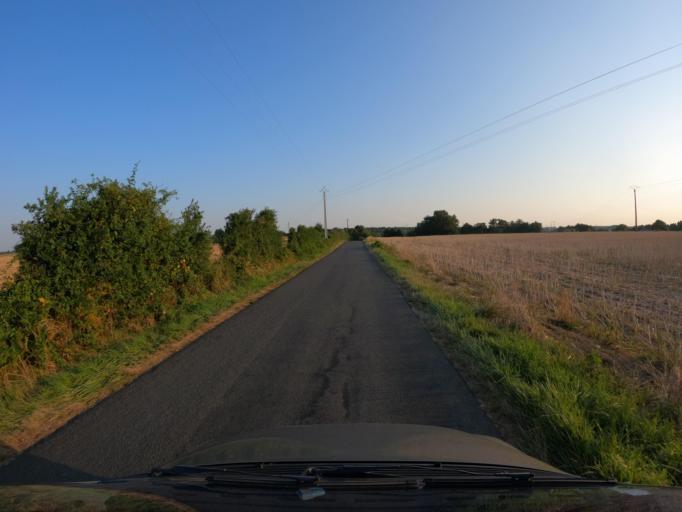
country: FR
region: Pays de la Loire
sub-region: Departement de la Sarthe
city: Parce-sur-Sarthe
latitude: 47.8868
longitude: -0.2198
